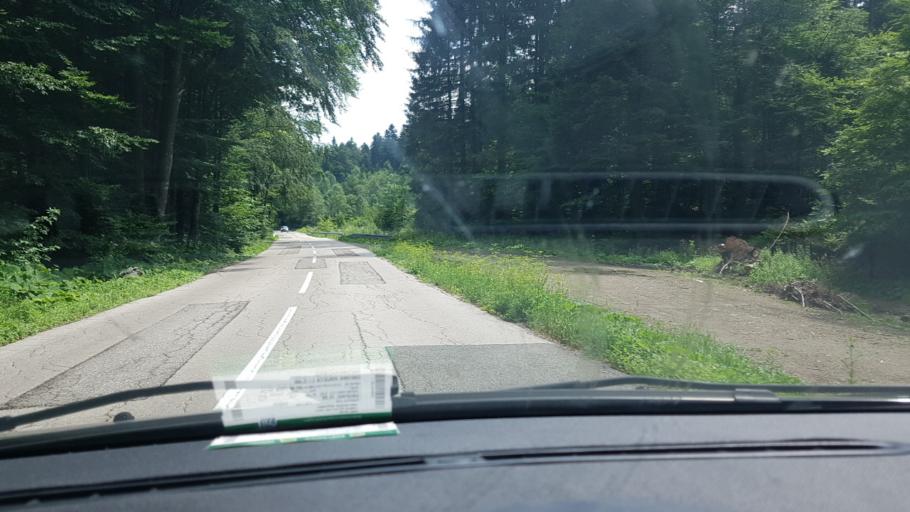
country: HR
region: Primorsko-Goranska
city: Hreljin
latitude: 45.3352
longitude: 14.6767
